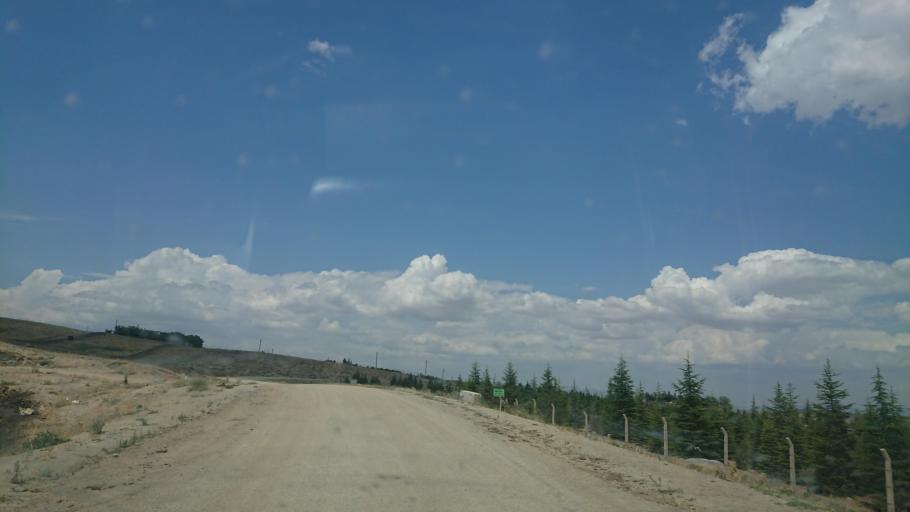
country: TR
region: Aksaray
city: Sariyahsi
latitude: 38.9479
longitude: 33.8811
